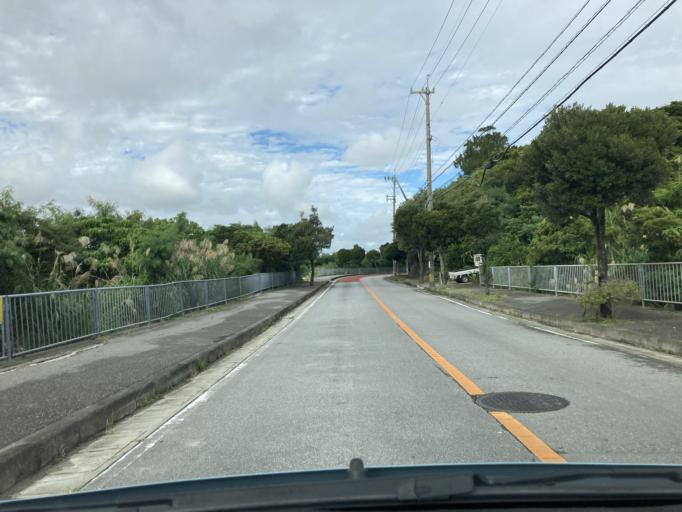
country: JP
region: Okinawa
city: Tomigusuku
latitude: 26.1818
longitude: 127.7461
